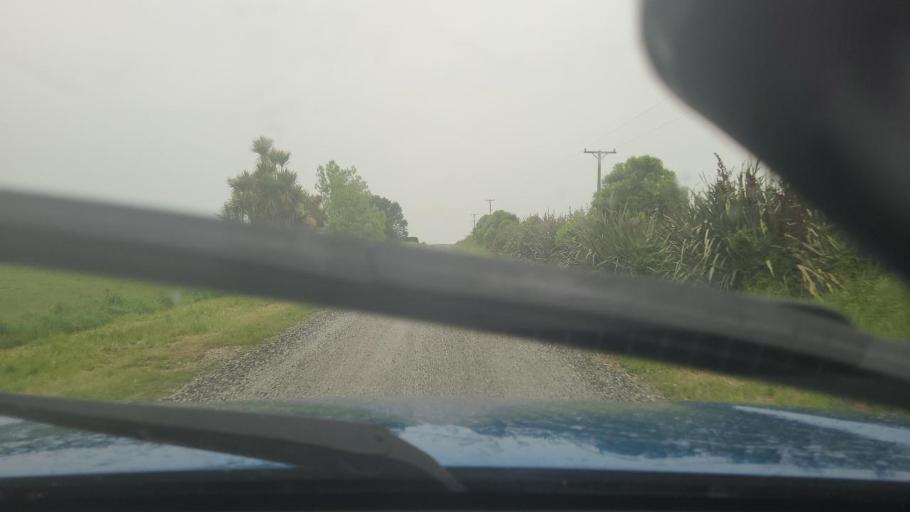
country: NZ
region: Southland
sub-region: Invercargill City
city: Invercargill
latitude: -46.4284
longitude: 168.4813
